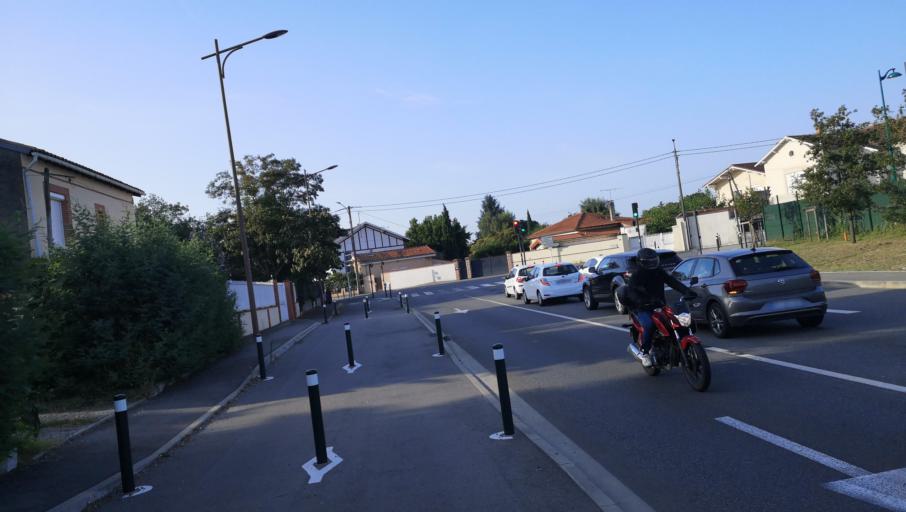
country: FR
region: Midi-Pyrenees
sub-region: Departement de la Haute-Garonne
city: Blagnac
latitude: 43.5939
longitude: 1.3934
